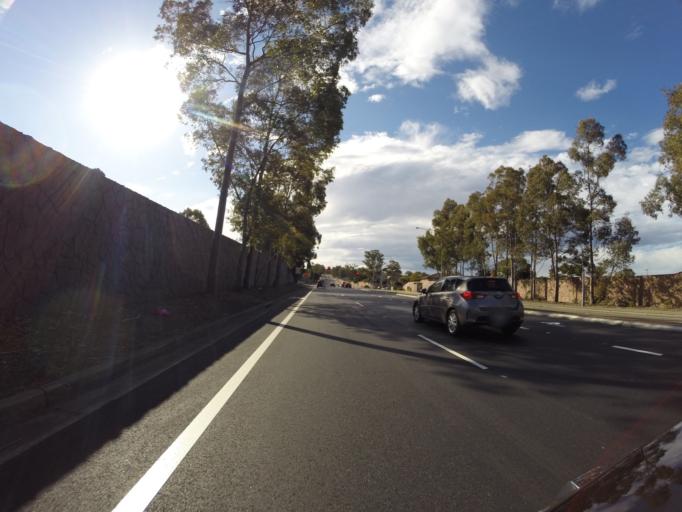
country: AU
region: New South Wales
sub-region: Fairfield
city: Cecil Park
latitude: -33.8699
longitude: 150.8700
